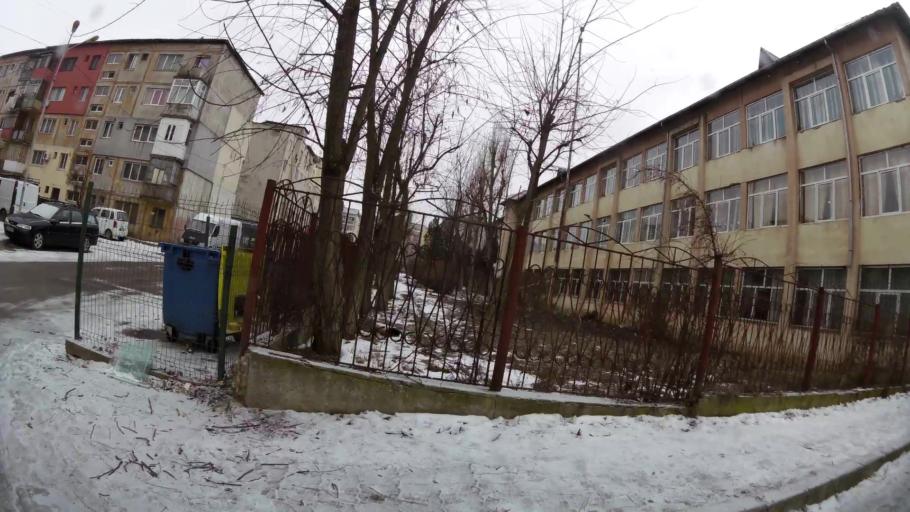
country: RO
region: Dambovita
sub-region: Municipiul Targoviste
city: Targoviste
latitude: 44.9329
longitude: 25.4487
